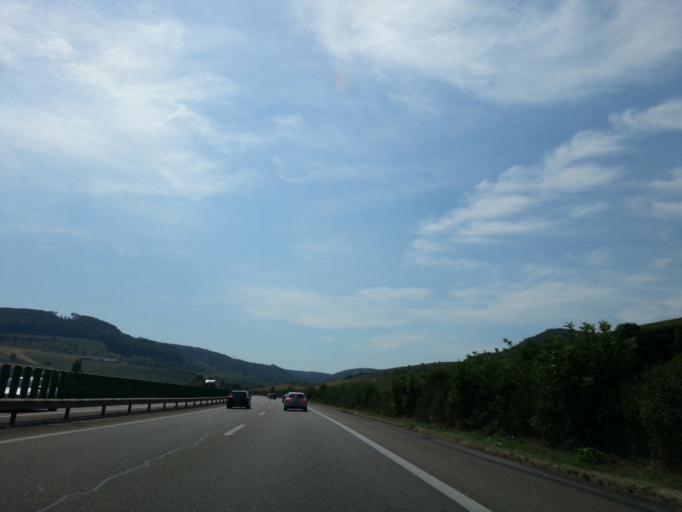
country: CH
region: Basel-Landschaft
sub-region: Bezirk Liestal
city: Arisdorf
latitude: 47.5184
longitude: 7.7542
